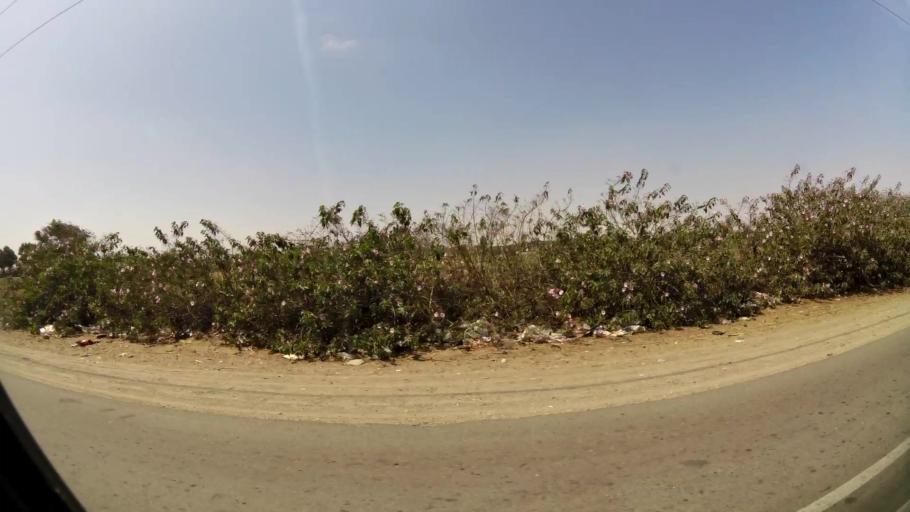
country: PE
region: La Libertad
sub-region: Provincia de Pacasmayo
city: San Pedro de Lloc
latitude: -7.4270
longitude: -79.4982
